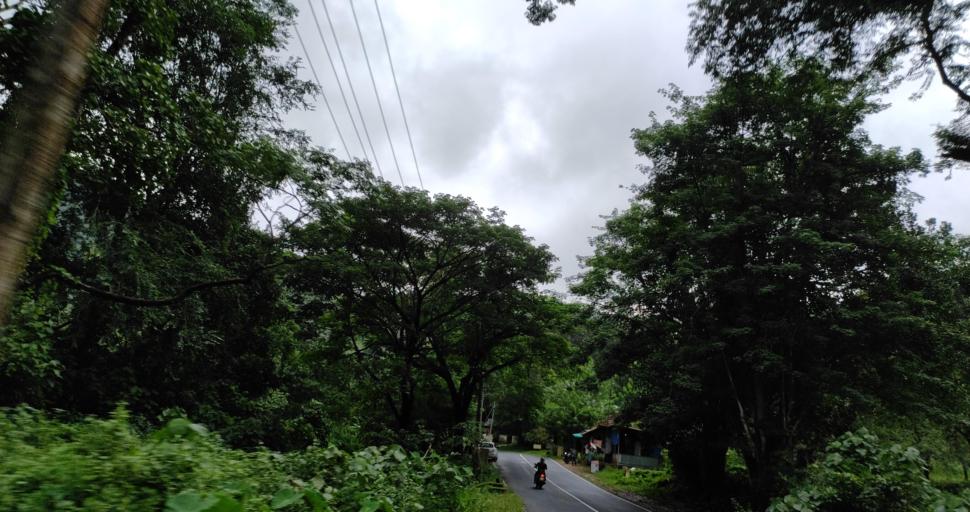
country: IN
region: Kerala
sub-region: Ernakulam
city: Angamali
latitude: 10.3000
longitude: 76.4500
